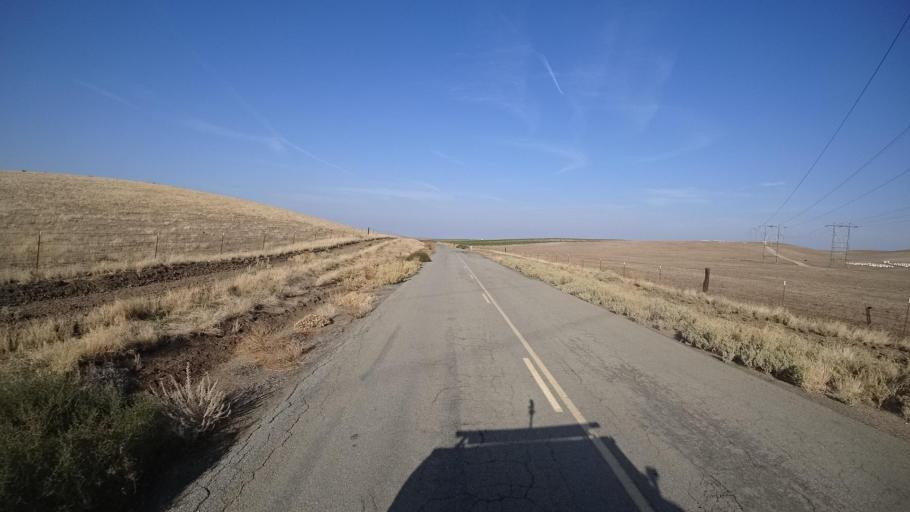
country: US
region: California
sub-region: Tulare County
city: Richgrove
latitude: 35.6398
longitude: -119.0429
